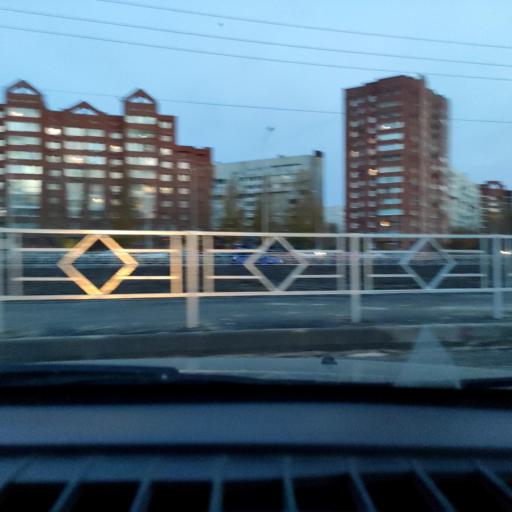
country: RU
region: Samara
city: Tol'yatti
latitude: 53.5456
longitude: 49.3245
